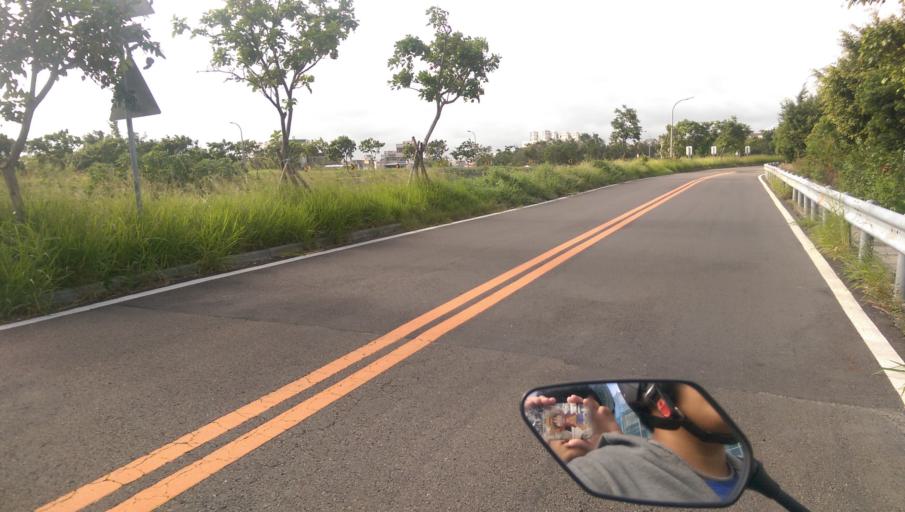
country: TW
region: Taiwan
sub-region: Hsinchu
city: Hsinchu
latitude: 24.8023
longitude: 120.9458
